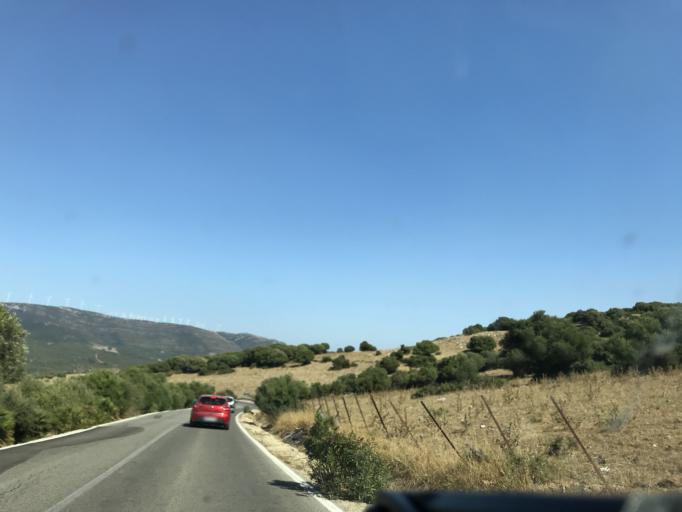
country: ES
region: Andalusia
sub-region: Provincia de Cadiz
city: Zahara de los Atunes
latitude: 36.1015
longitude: -5.7220
